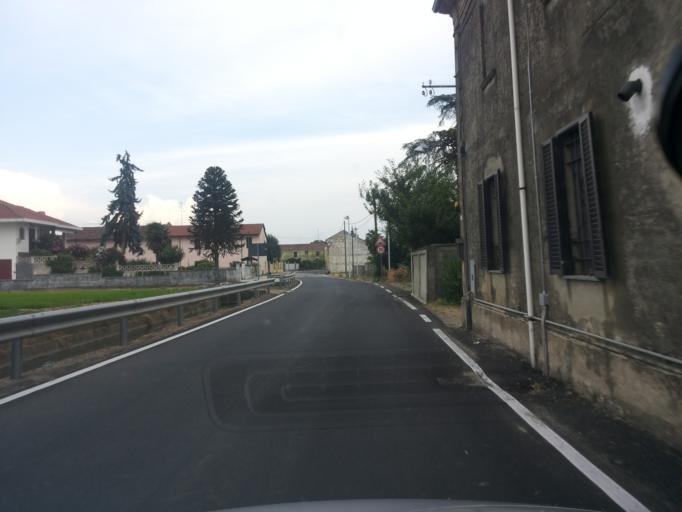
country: IT
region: Piedmont
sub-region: Provincia di Vercelli
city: Pezzana
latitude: 45.2670
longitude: 8.4846
